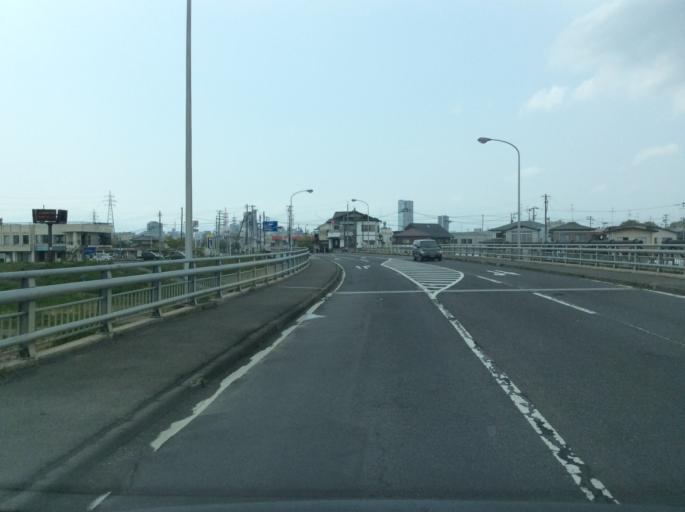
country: JP
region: Fukushima
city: Koriyama
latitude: 37.3867
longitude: 140.4011
